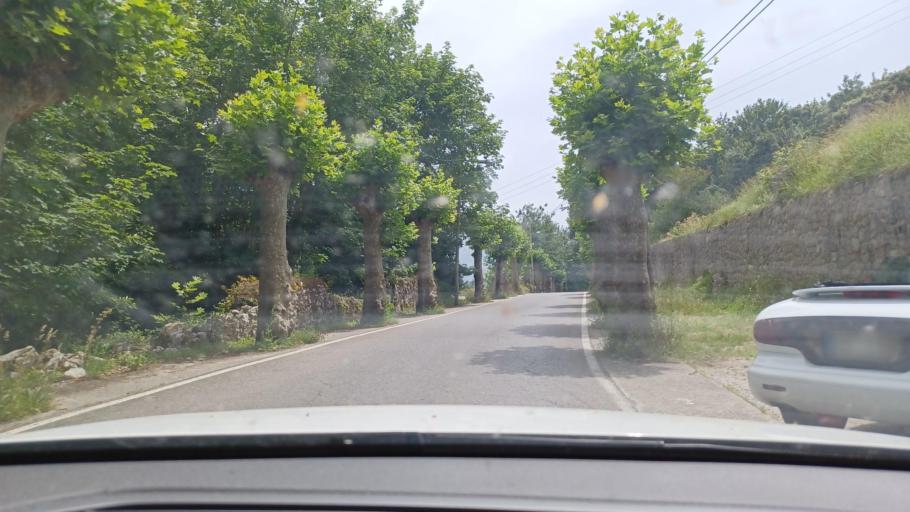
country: ES
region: Asturias
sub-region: Province of Asturias
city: Llanes
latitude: 43.4182
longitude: -4.7567
